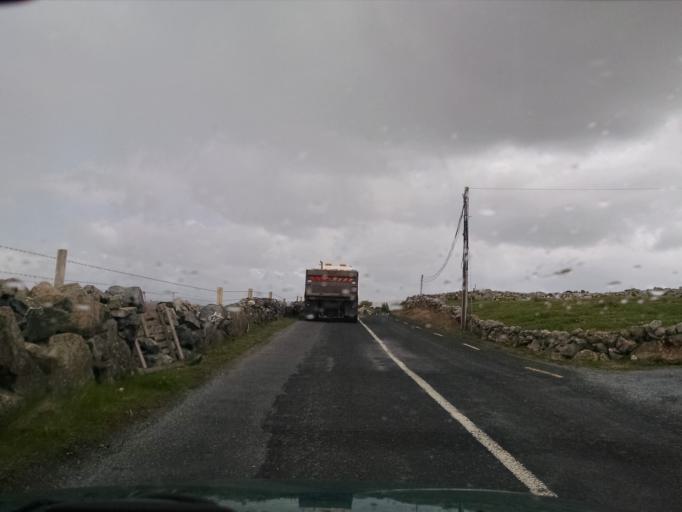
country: IE
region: Connaught
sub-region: County Galway
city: Oughterard
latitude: 53.3158
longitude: -9.5520
